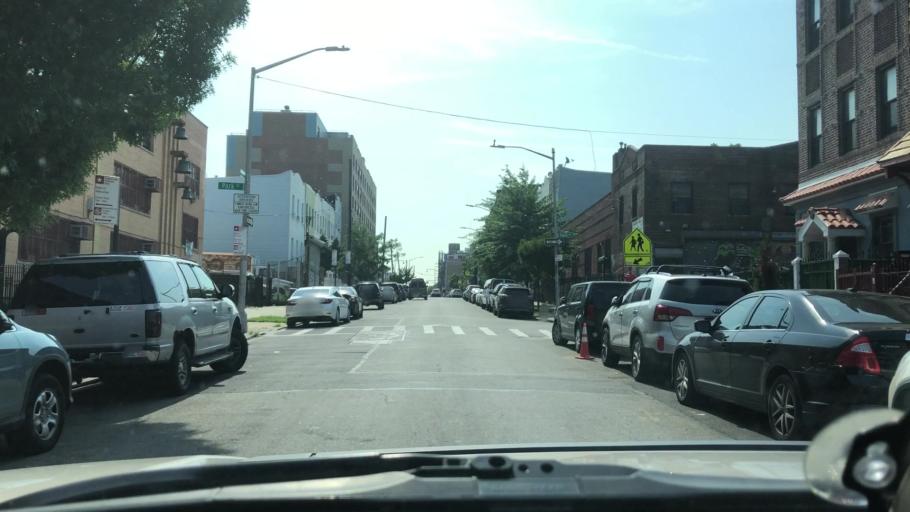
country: US
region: New York
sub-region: Queens County
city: Long Island City
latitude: 40.7004
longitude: -73.9381
